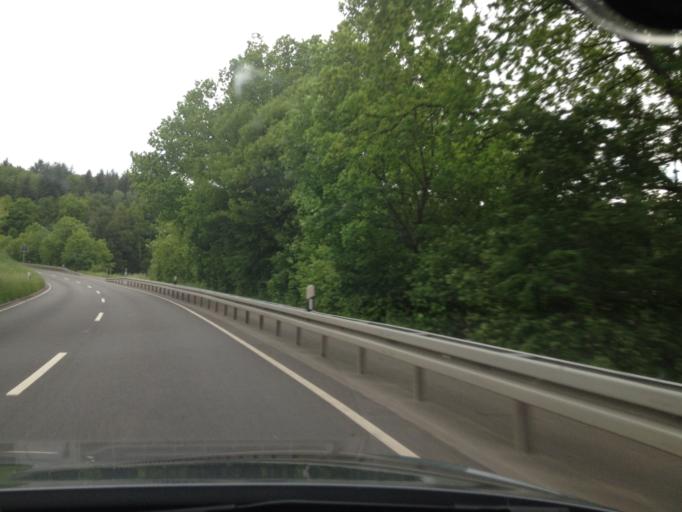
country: DE
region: Saarland
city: Kirkel
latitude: 49.2968
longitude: 7.2128
